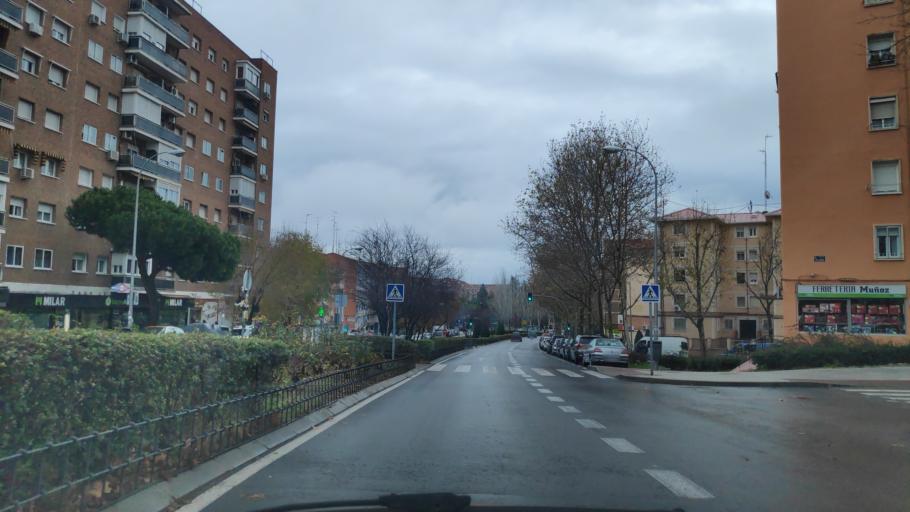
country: ES
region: Madrid
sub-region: Provincia de Madrid
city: Hortaleza
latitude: 40.4725
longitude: -3.6517
